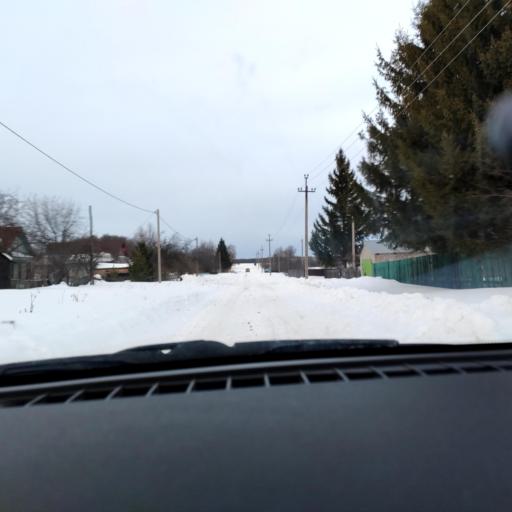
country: RU
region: Bashkortostan
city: Iglino
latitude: 54.7369
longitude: 56.5388
